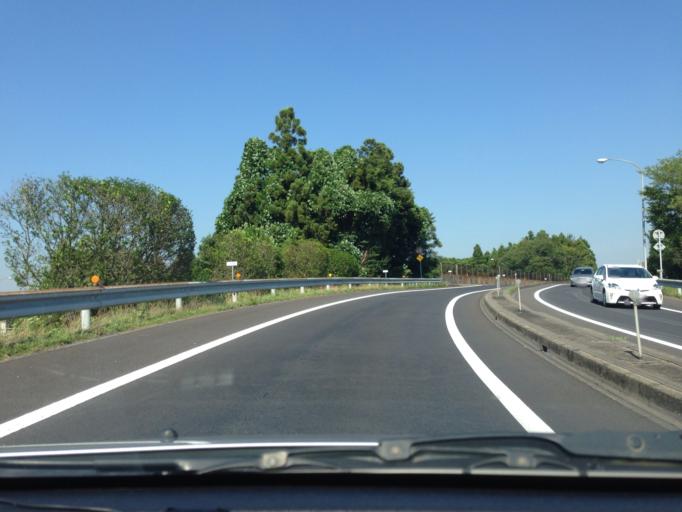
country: JP
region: Ibaraki
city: Naka
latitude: 36.0568
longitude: 140.1564
